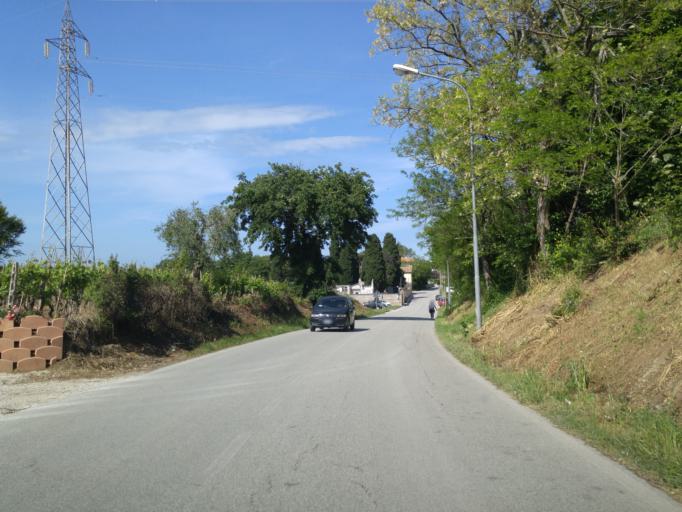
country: IT
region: The Marches
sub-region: Provincia di Pesaro e Urbino
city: San Costanzo
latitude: 43.7585
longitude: 13.0646
